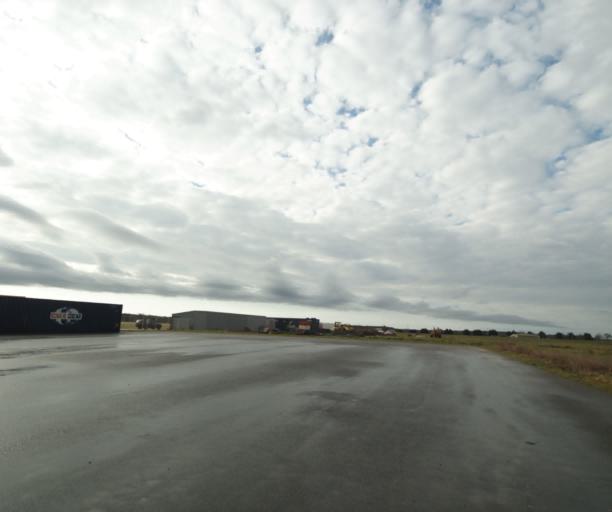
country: FR
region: Auvergne
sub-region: Departement de l'Allier
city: Toulon-sur-Allier
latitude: 46.5378
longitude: 3.4279
